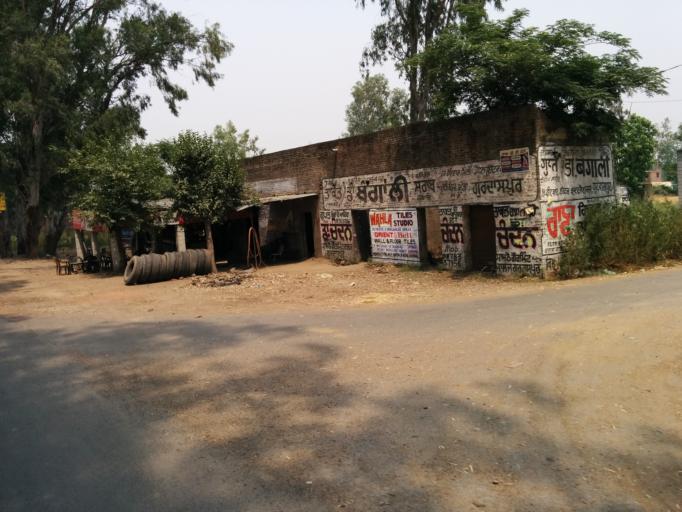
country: IN
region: Punjab
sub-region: Gurdaspur
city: Dhariwal
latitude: 31.9333
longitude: 75.3061
